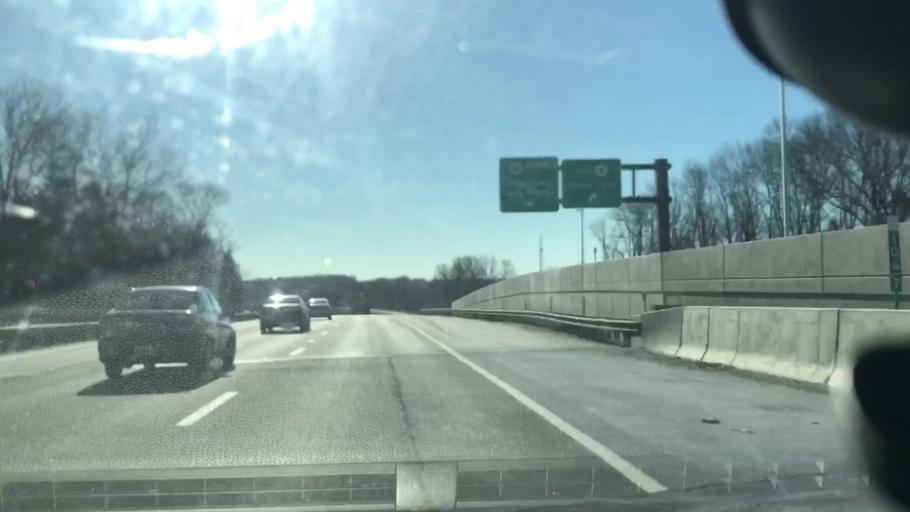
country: US
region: New Jersey
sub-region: Monmouth County
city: Tinton Falls
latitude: 40.2876
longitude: -74.0907
